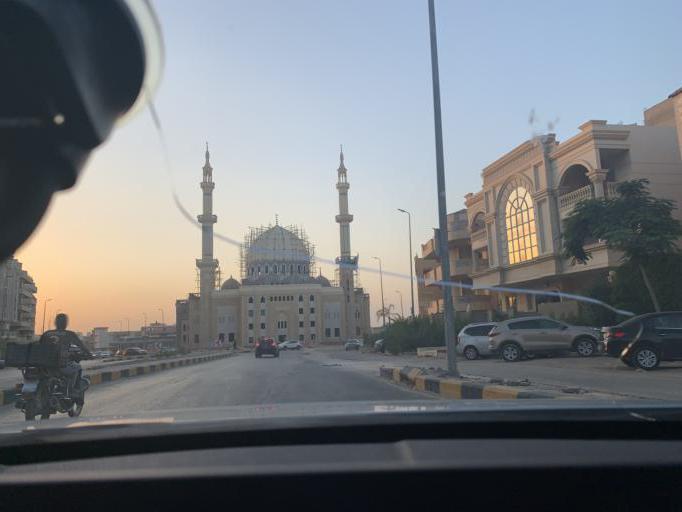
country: EG
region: Muhafazat al Qahirah
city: Cairo
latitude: 30.0045
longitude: 31.4580
